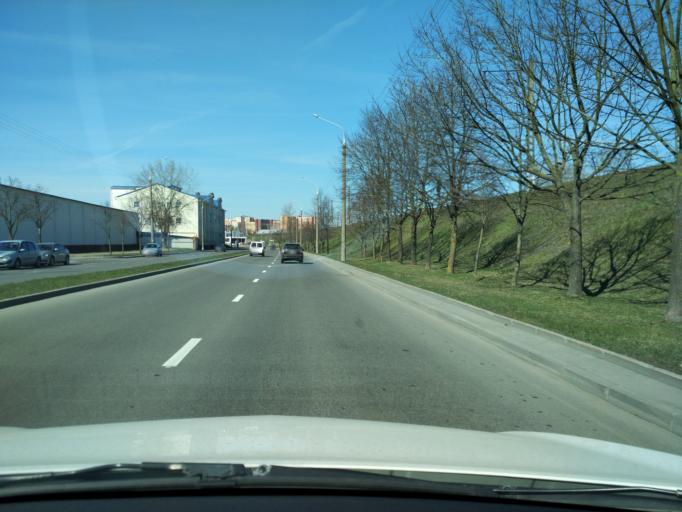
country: BY
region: Minsk
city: Minsk
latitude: 53.8798
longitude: 27.5627
